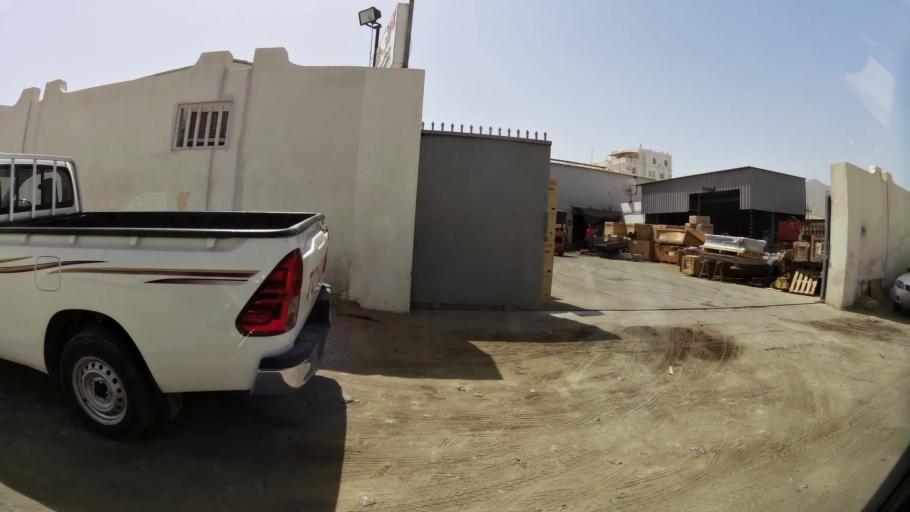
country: OM
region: Muhafazat Masqat
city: Bawshar
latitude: 23.5953
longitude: 58.4453
